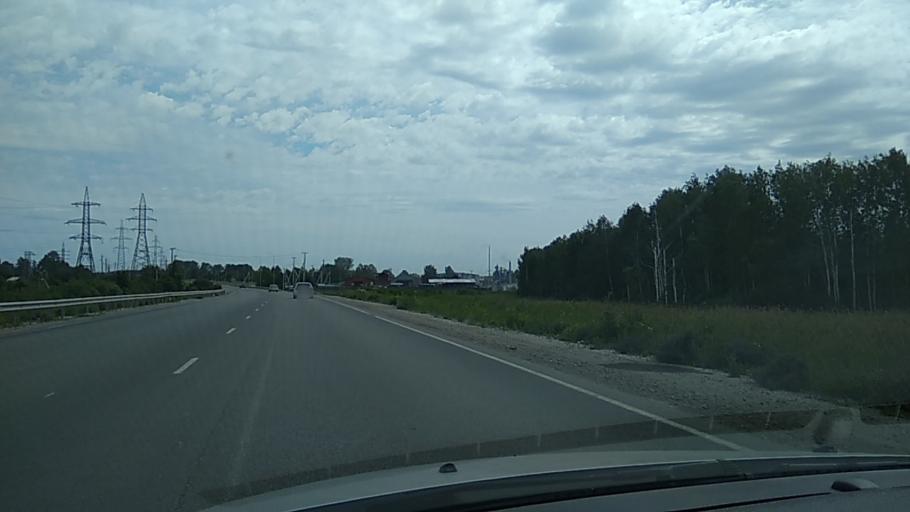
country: RU
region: Sverdlovsk
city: Verkhnyaya Pyshma
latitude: 56.9489
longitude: 60.5951
